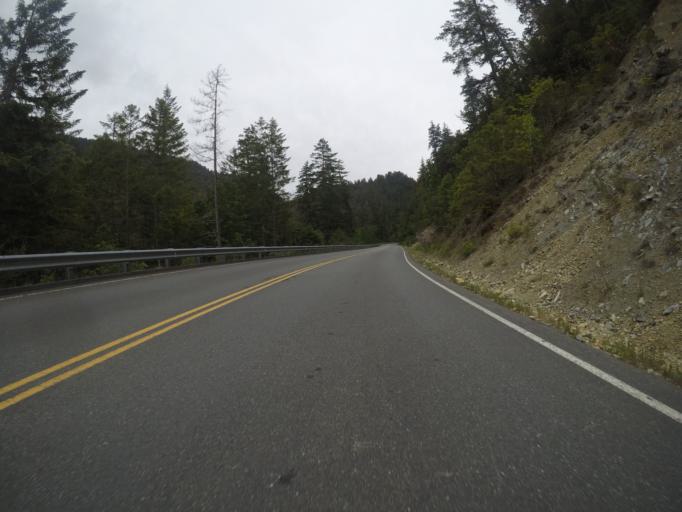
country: US
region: California
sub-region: Del Norte County
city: Bertsch-Oceanview
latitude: 41.7188
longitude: -123.9466
